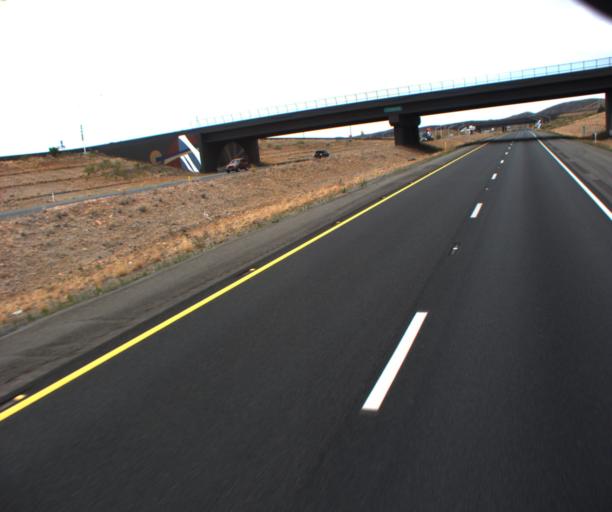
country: US
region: Arizona
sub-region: Yavapai County
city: Cordes Lakes
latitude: 34.3348
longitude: -112.1198
